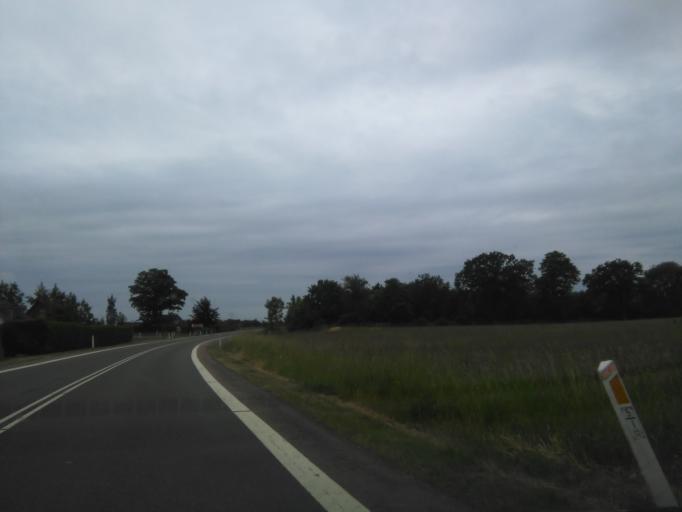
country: DK
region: Capital Region
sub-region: Bornholm Kommune
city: Akirkeby
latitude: 55.1114
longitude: 14.9120
